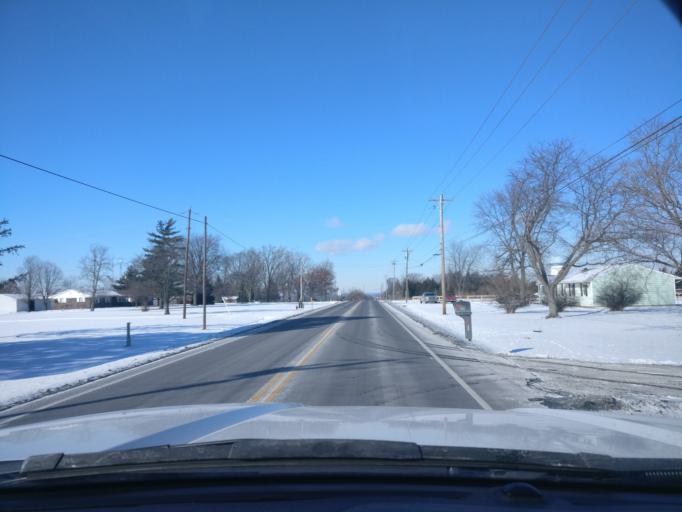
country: US
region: Ohio
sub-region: Warren County
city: Hunter
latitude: 39.5047
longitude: -84.2627
